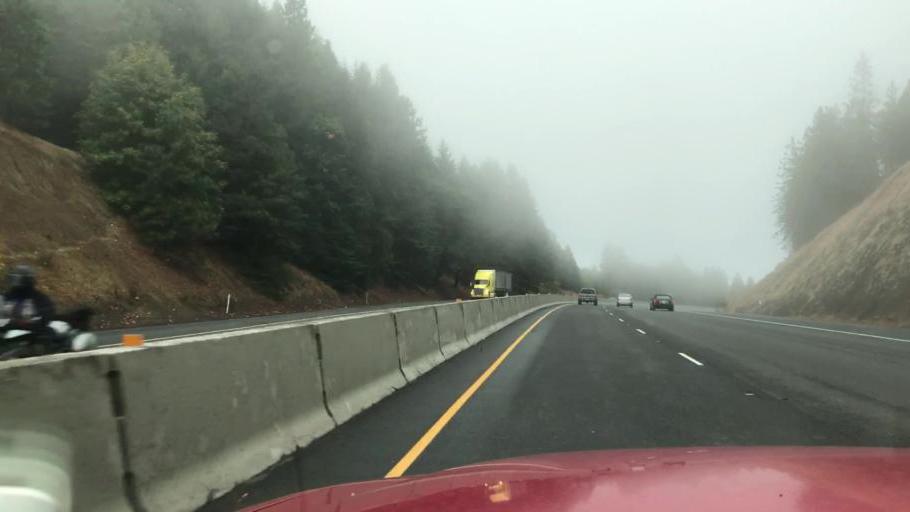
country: US
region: Oregon
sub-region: Josephine County
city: Merlin
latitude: 42.6025
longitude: -123.3834
